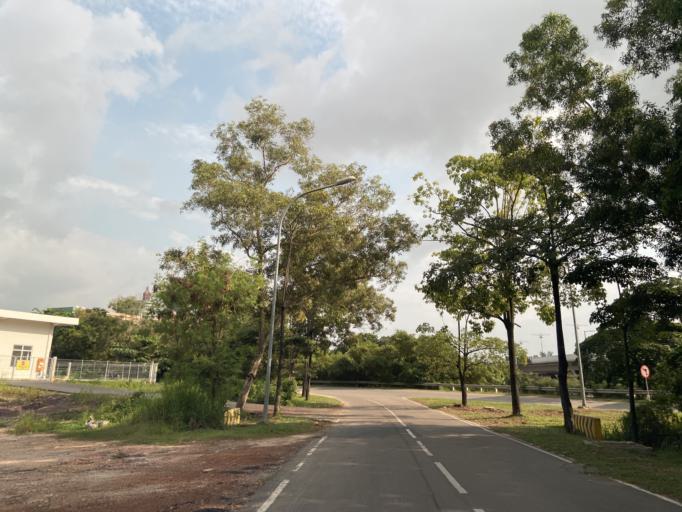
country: SG
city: Singapore
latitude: 1.1222
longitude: 104.0188
